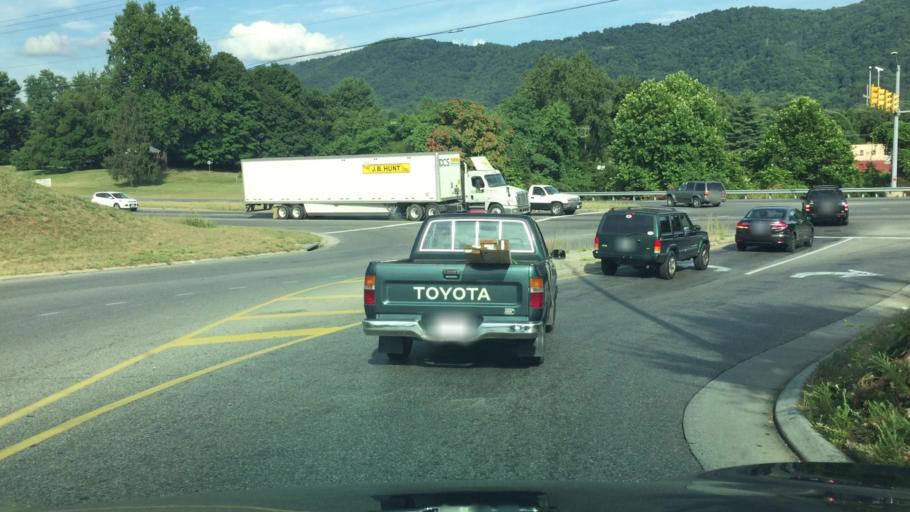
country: US
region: Virginia
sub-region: Botetourt County
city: Laymantown
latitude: 37.3234
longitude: -79.8720
